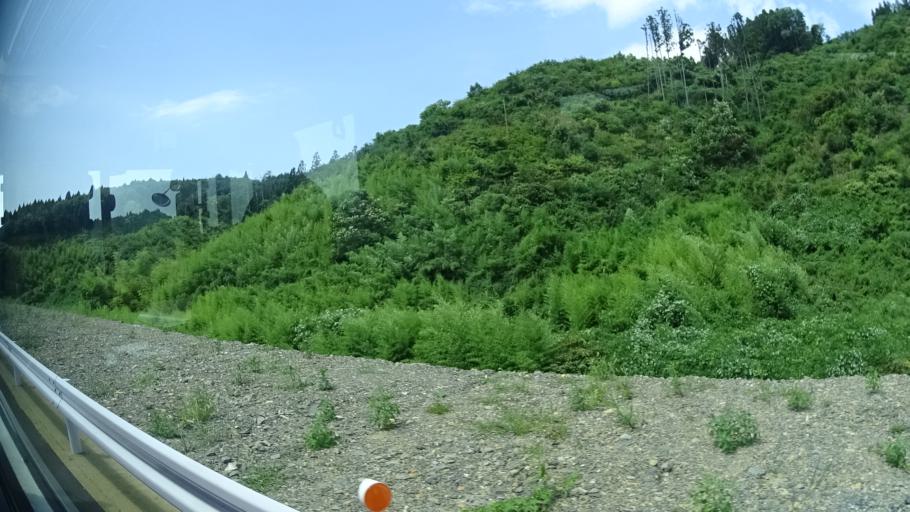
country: JP
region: Miyagi
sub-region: Oshika Gun
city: Onagawa Cho
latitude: 38.6479
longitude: 141.4316
